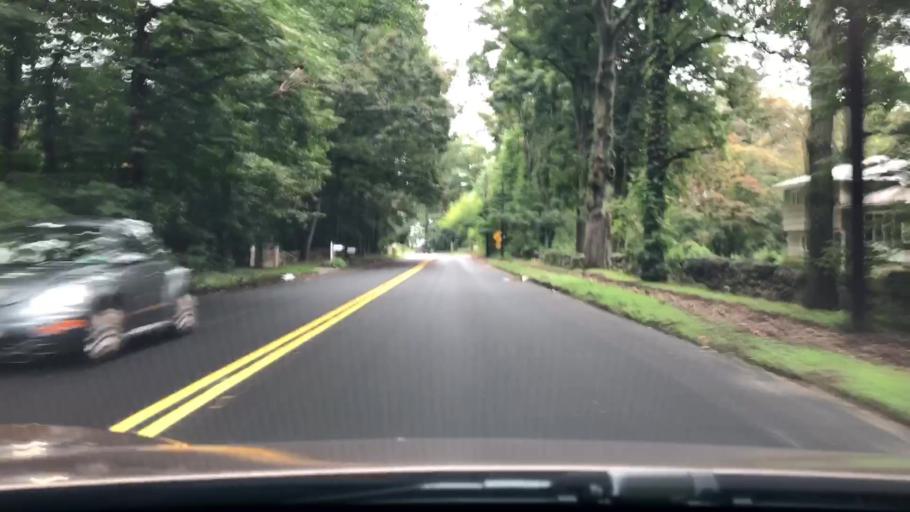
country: US
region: Connecticut
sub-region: Fairfield County
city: New Canaan
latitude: 41.1291
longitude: -73.4553
